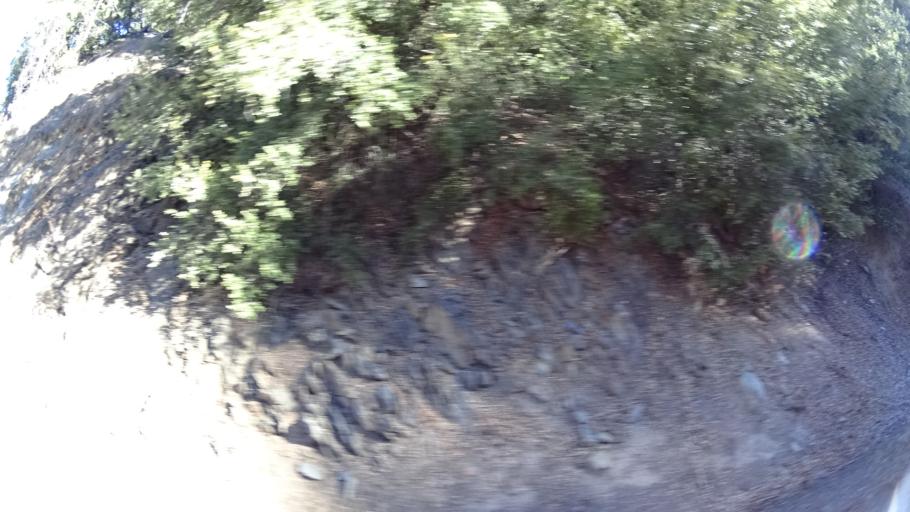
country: US
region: California
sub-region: Trinity County
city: Weaverville
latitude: 41.2221
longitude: -123.0125
